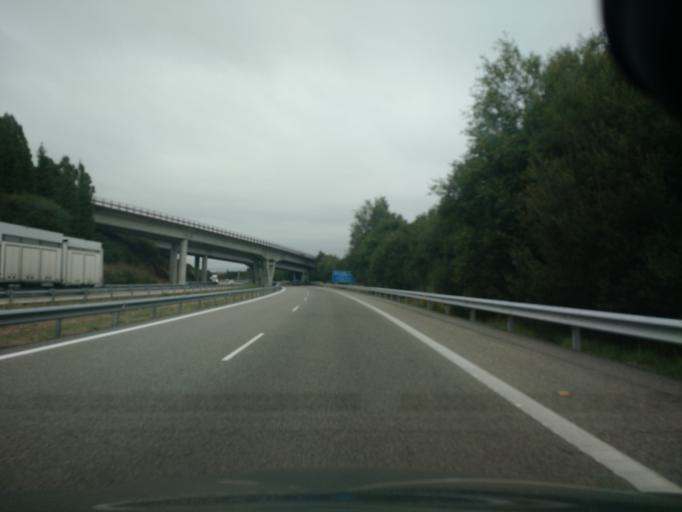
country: ES
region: Galicia
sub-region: Provincia da Coruna
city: Santiago de Compostela
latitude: 42.9018
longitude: -8.4980
